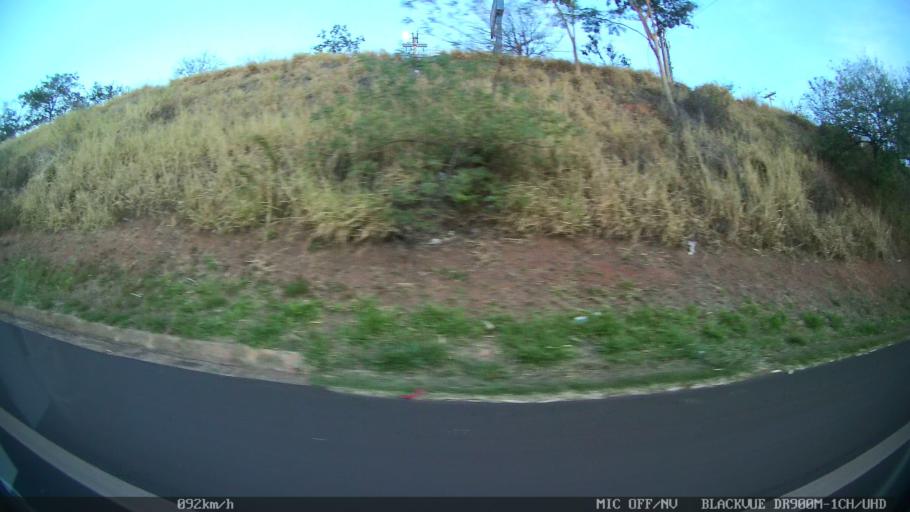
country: BR
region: Sao Paulo
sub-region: Catanduva
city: Catanduva
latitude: -21.1288
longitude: -49.0087
